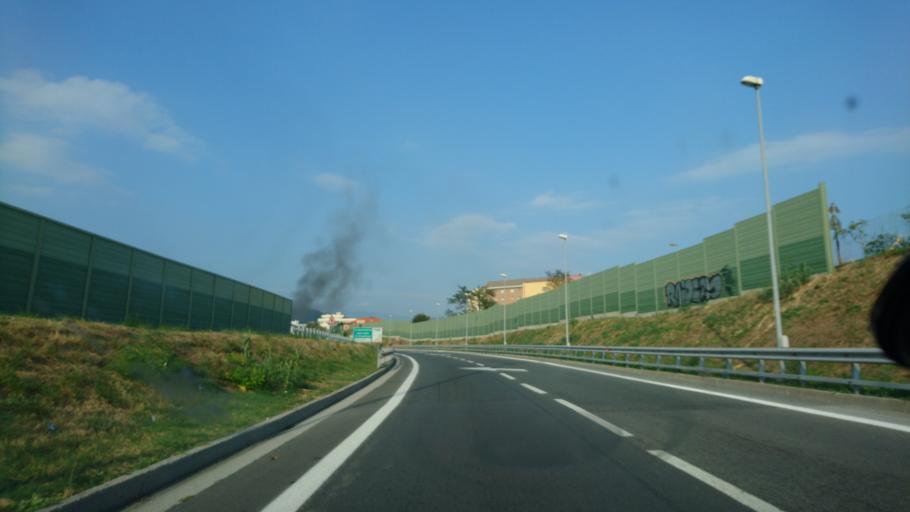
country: IT
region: Liguria
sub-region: Provincia di Savona
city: Valleggia
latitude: 44.2901
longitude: 8.4449
